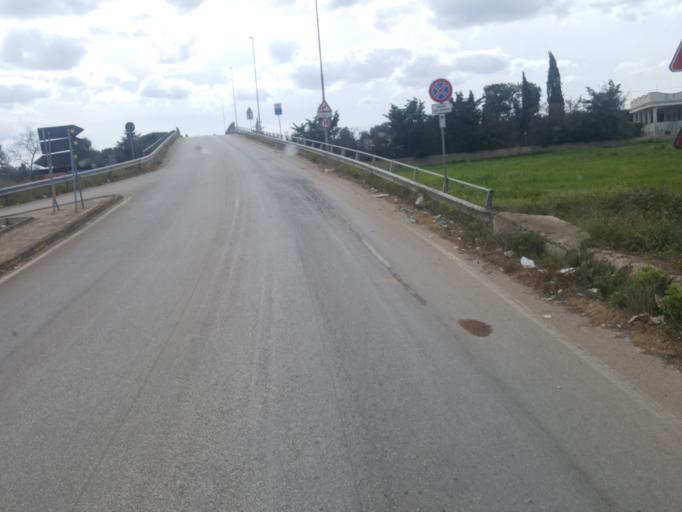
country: IT
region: Apulia
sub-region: Provincia di Barletta - Andria - Trani
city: Bisceglie
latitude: 41.2245
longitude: 16.5050
